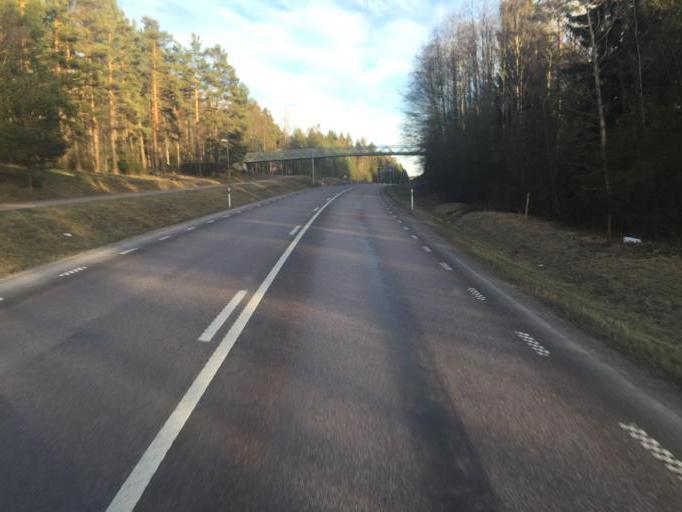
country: SE
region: Dalarna
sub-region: Borlange Kommun
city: Borlaenge
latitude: 60.5122
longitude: 15.3807
